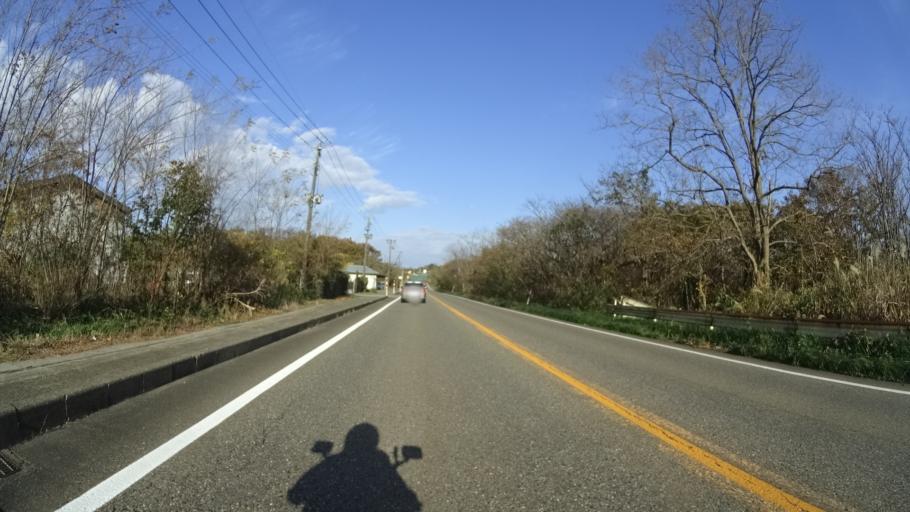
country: JP
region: Niigata
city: Joetsu
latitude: 37.2606
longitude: 138.3704
